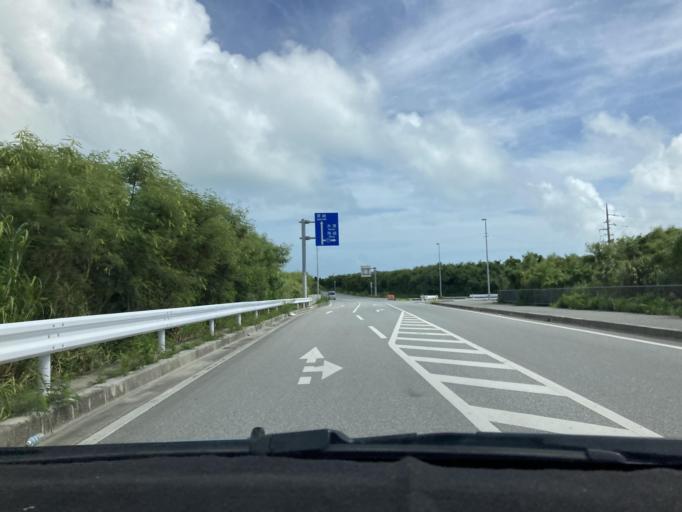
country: JP
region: Okinawa
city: Ginowan
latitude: 26.2111
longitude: 127.7635
